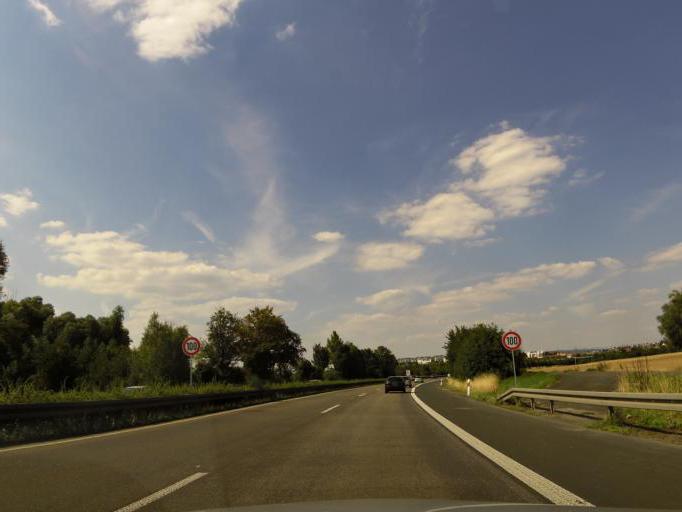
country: DE
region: Hesse
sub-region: Regierungsbezirk Darmstadt
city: Bad Homburg vor der Hoehe
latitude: 50.1726
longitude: 8.6496
